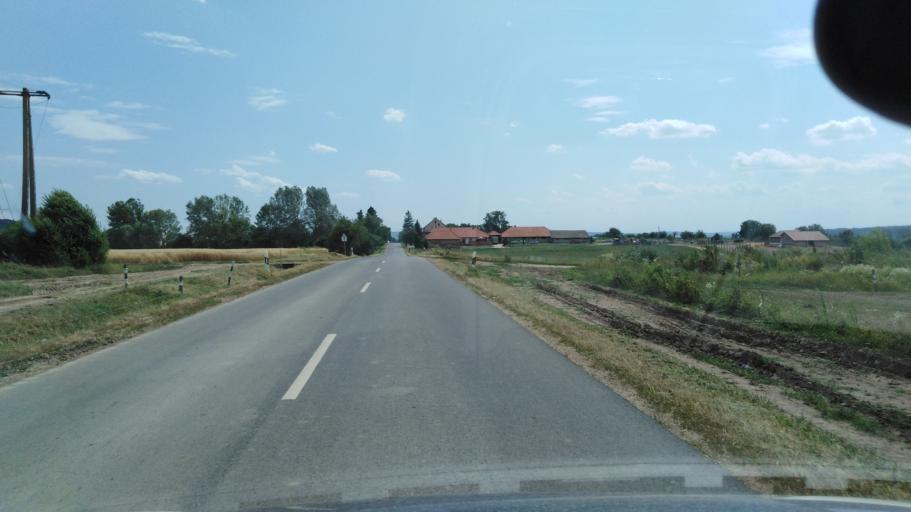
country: HU
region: Nograd
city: Szecseny
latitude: 48.1540
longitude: 19.5333
